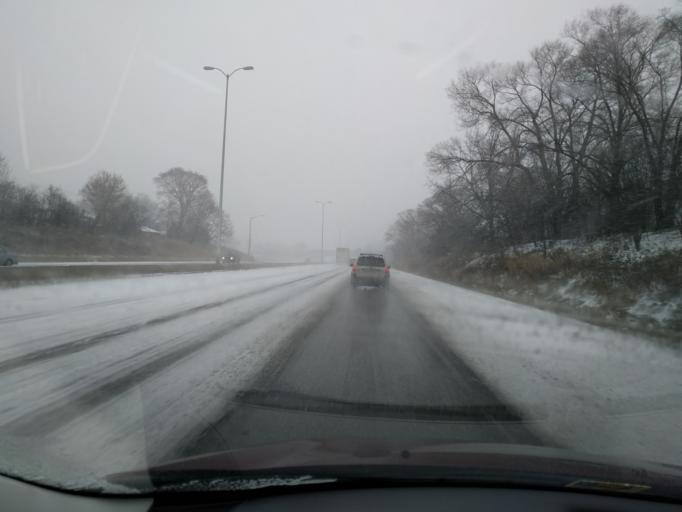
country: US
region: Wisconsin
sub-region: Waukesha County
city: Butler
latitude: 43.1224
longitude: -88.0156
